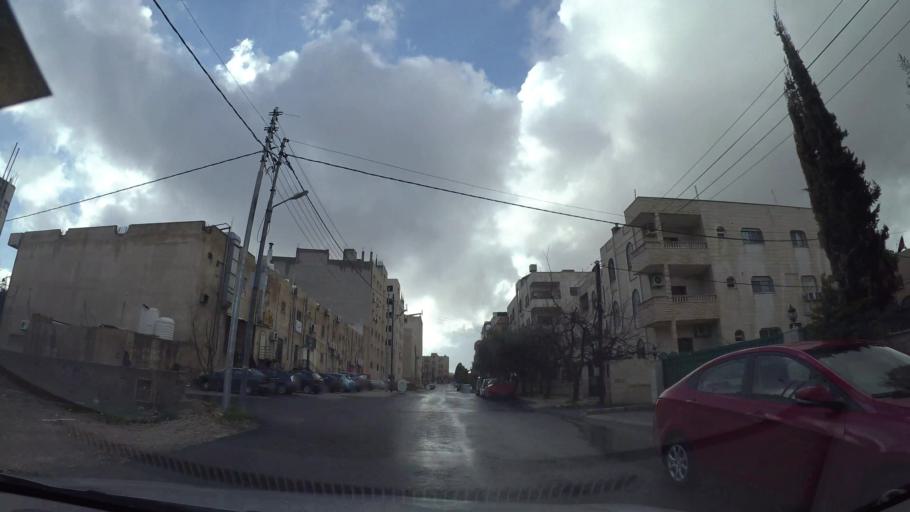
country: JO
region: Amman
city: Al Jubayhah
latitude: 32.0293
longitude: 35.8663
